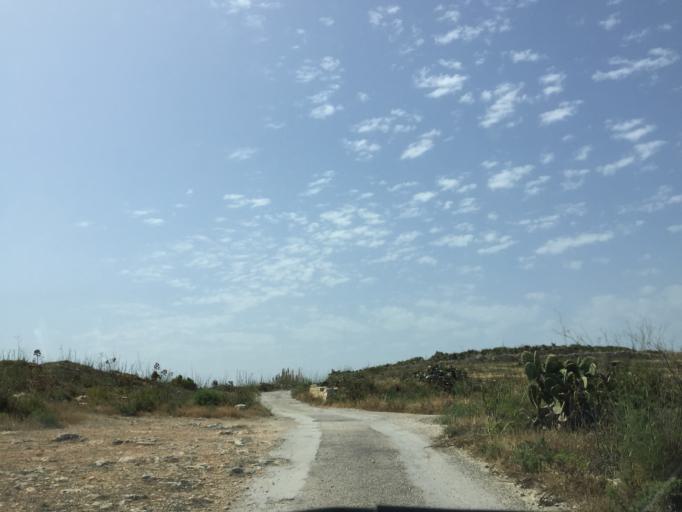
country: MT
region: In-Nadur
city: Nadur
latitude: 36.0612
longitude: 14.2904
